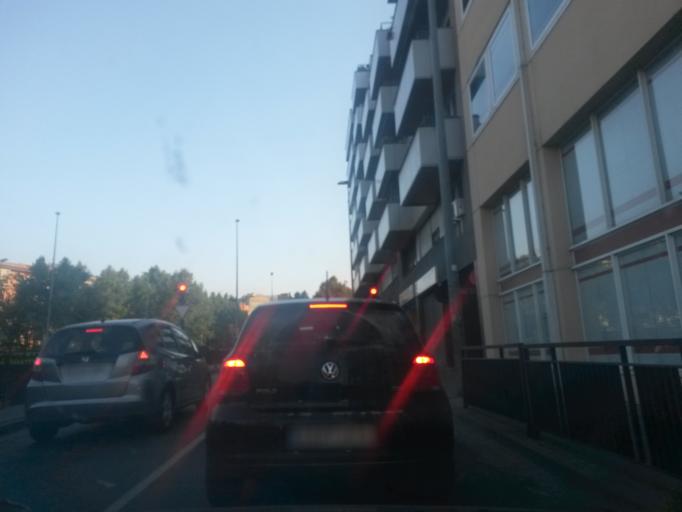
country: ES
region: Catalonia
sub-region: Provincia de Girona
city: Girona
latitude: 41.9795
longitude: 2.8109
